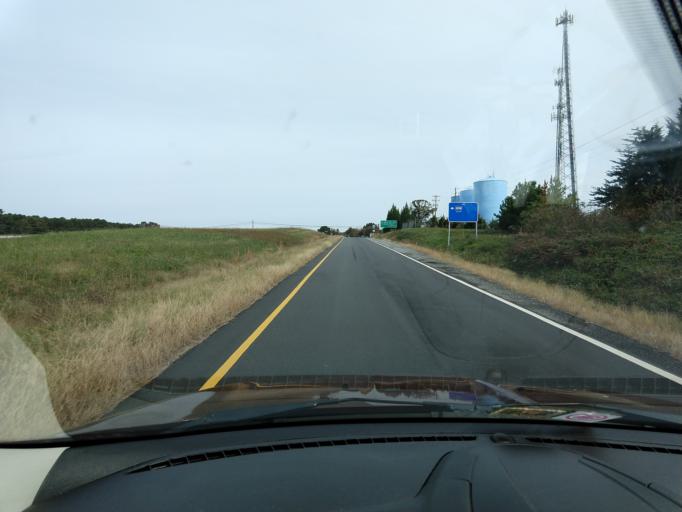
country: US
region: Virginia
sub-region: Pittsylvania County
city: Gretna
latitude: 36.9521
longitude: -79.3783
